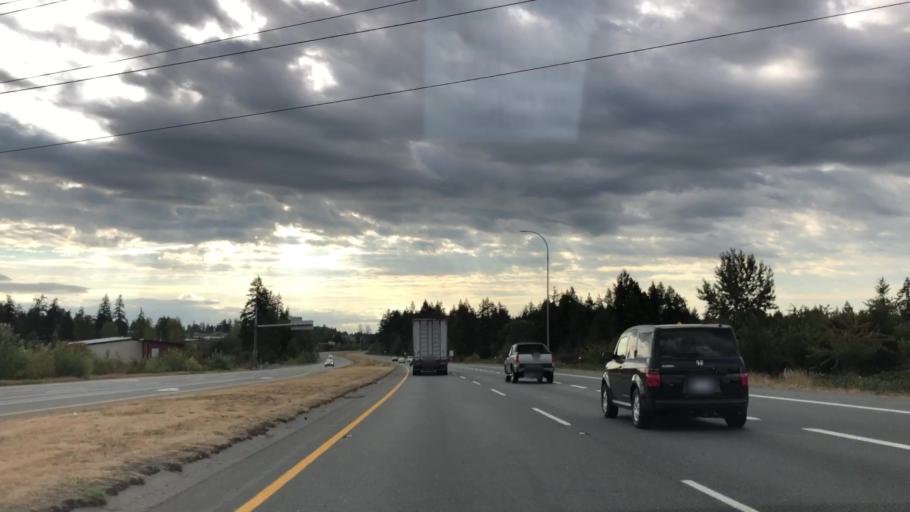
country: CA
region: British Columbia
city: Nanaimo
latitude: 49.1877
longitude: -124.0009
